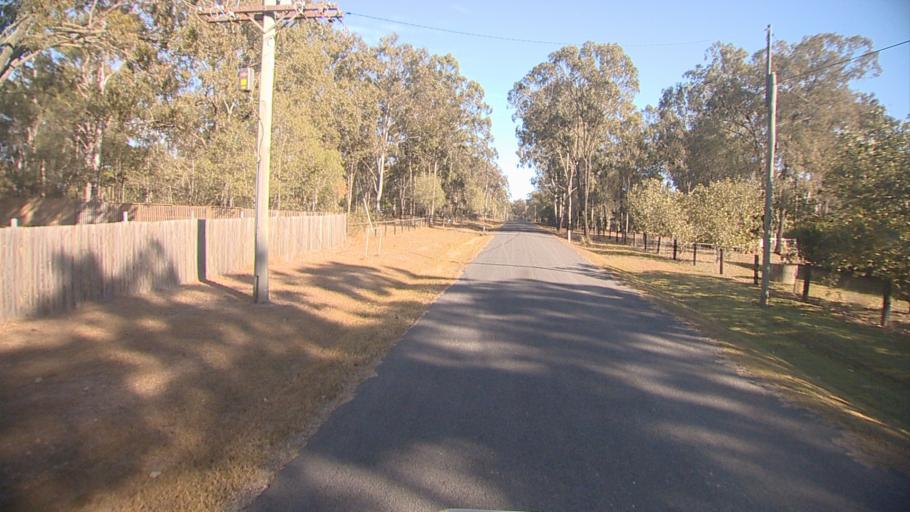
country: AU
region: Queensland
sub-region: Gold Coast
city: Ormeau Hills
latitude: -27.8273
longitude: 153.1718
